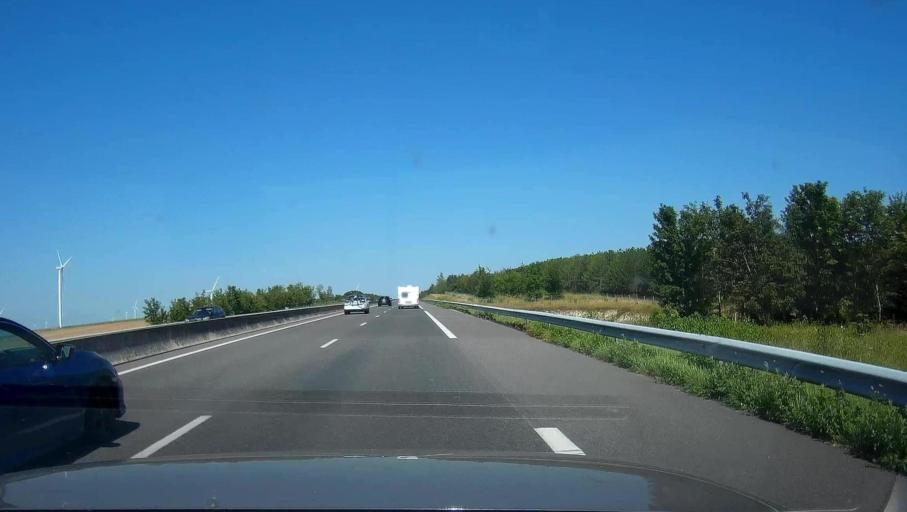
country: FR
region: Champagne-Ardenne
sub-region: Departement de l'Aube
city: Arcis-sur-Aube
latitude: 48.5775
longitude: 4.1889
